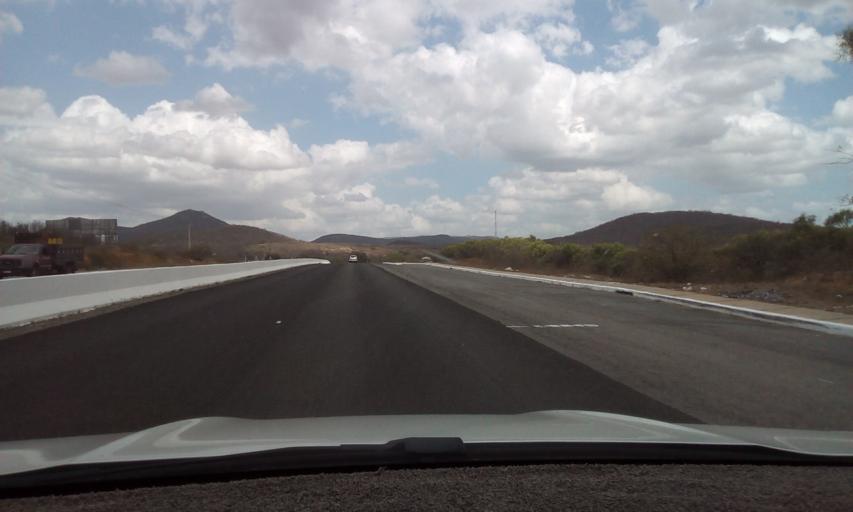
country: BR
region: Pernambuco
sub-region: Toritama
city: Toritama
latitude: -8.1146
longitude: -36.0094
